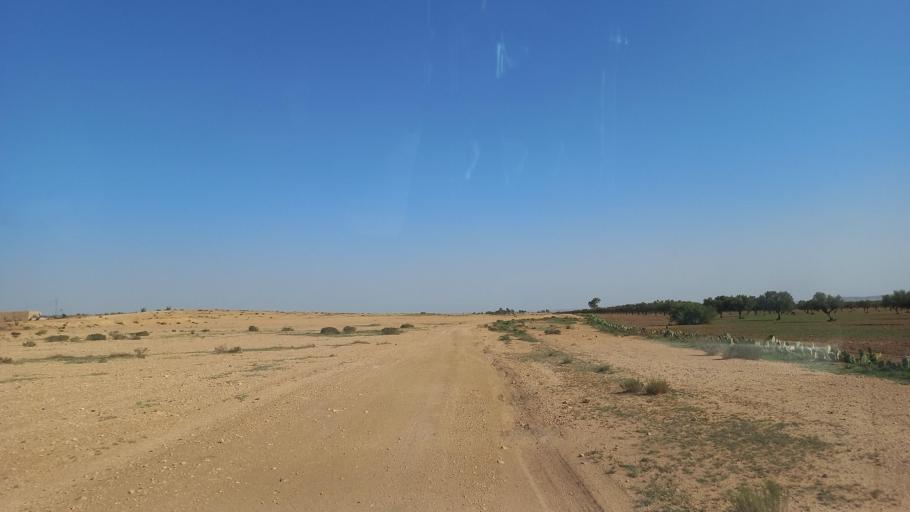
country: TN
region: Al Qasrayn
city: Kasserine
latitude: 35.3119
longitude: 9.0179
